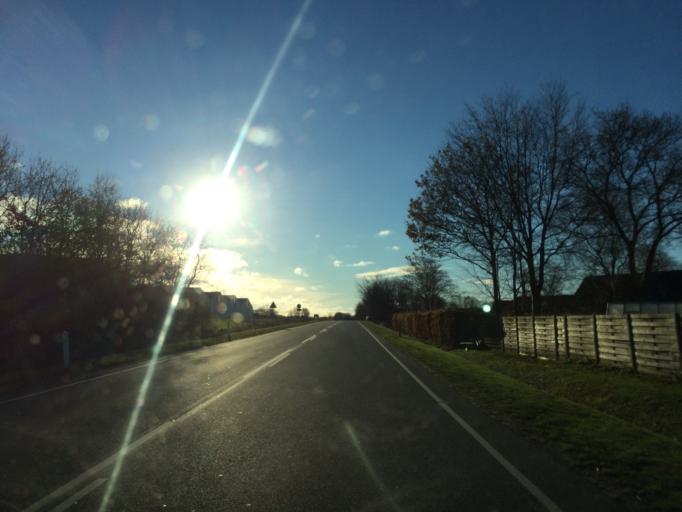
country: DK
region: Central Jutland
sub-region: Herning Kommune
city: Kibaek
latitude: 56.0311
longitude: 8.8594
